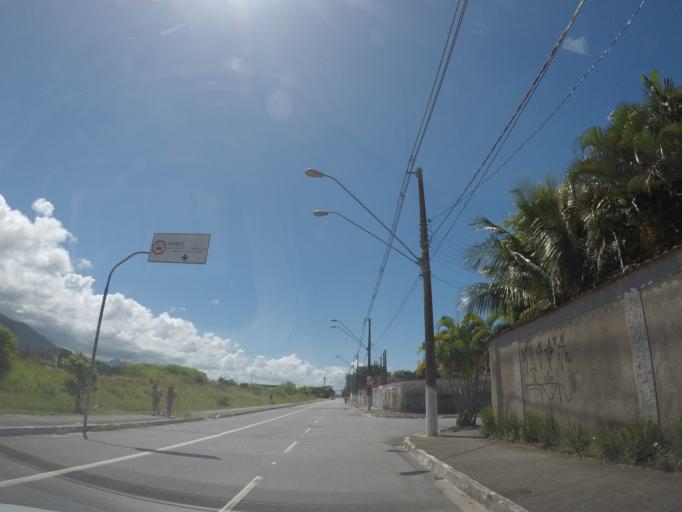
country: BR
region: Sao Paulo
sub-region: Mongagua
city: Mongagua
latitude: -24.0797
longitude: -46.5945
